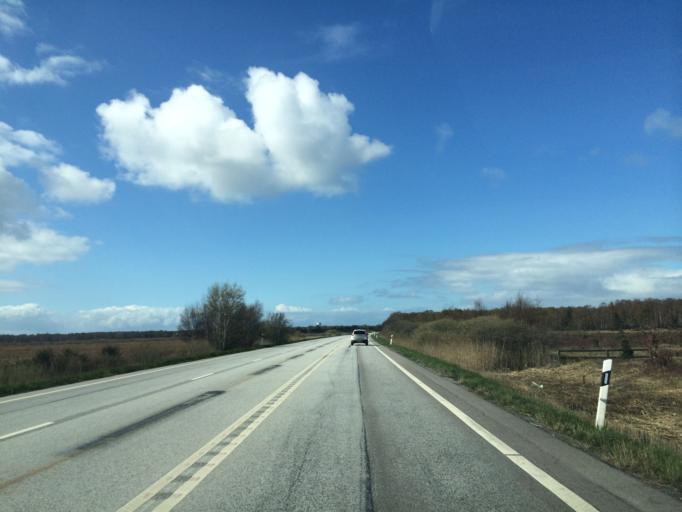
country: SE
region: Skane
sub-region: Vellinge Kommun
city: Skanor med Falsterbo
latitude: 55.4050
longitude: 12.8842
